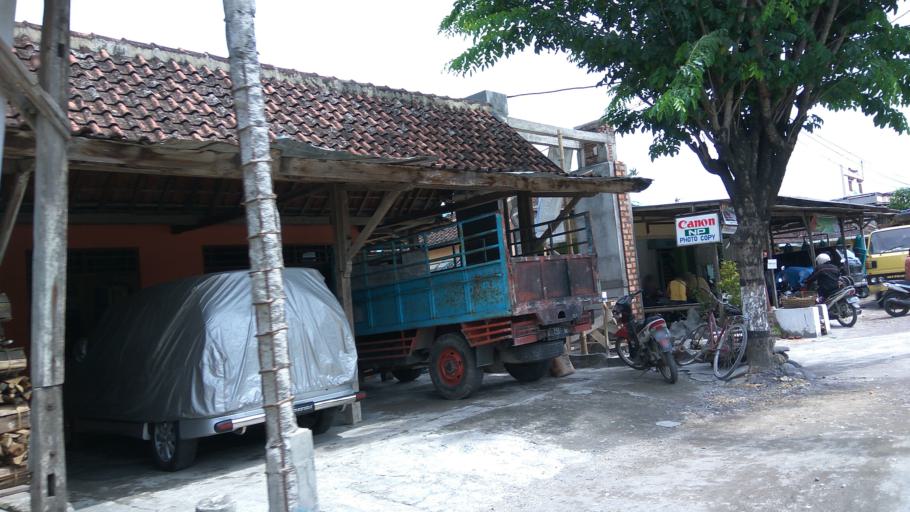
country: ID
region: Central Java
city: Mranggen
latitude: -7.0628
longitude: 110.6664
